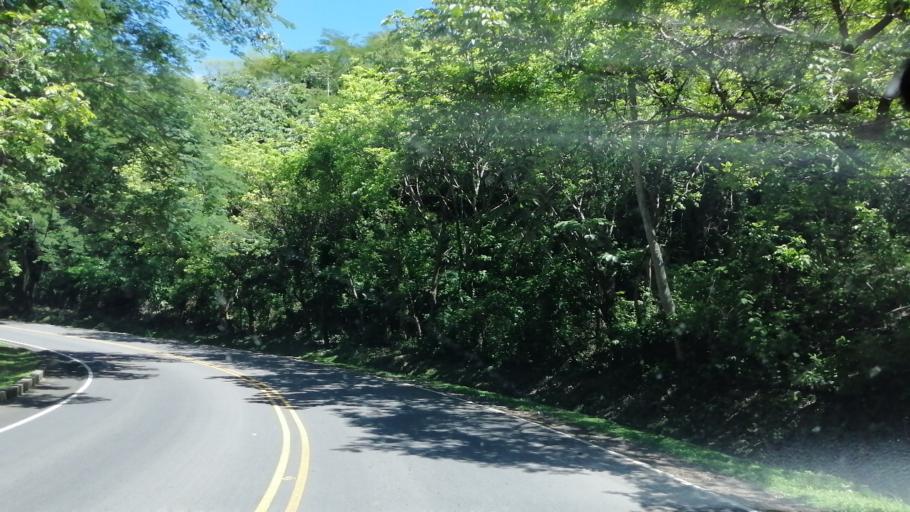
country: SV
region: Morazan
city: Cacaopera
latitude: 13.7996
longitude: -88.1482
